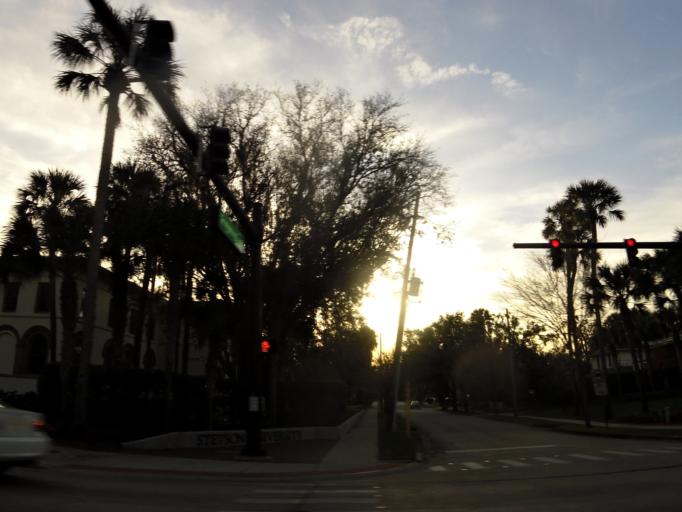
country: US
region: Florida
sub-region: Volusia County
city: DeLand
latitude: 29.0353
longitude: -81.3036
